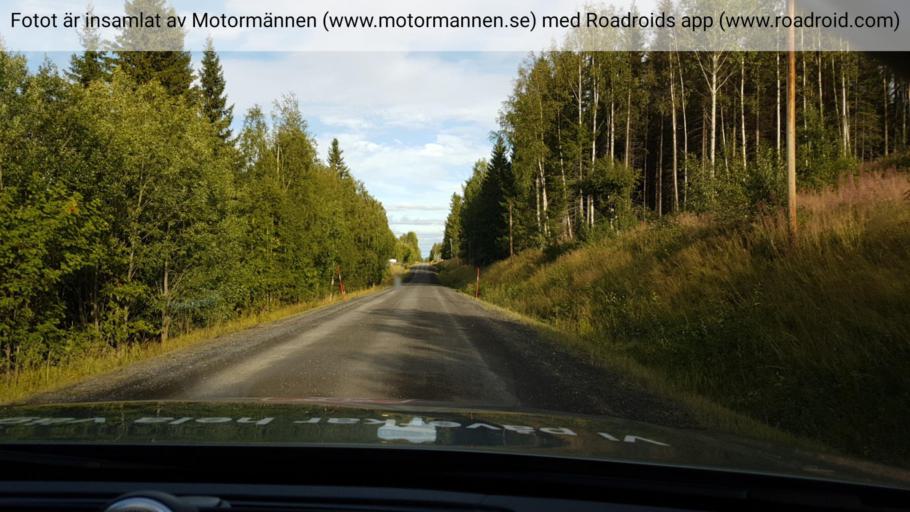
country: SE
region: Jaemtland
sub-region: Stroemsunds Kommun
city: Stroemsund
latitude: 64.1427
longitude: 15.7137
